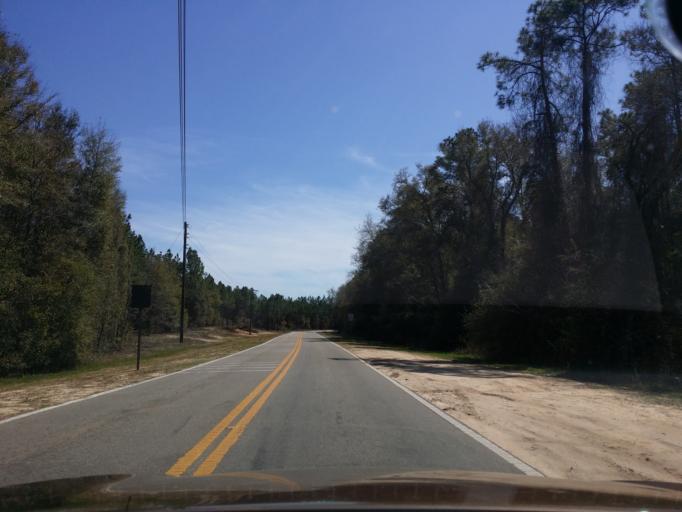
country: US
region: Florida
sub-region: Leon County
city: Woodville
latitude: 30.3702
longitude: -84.1263
